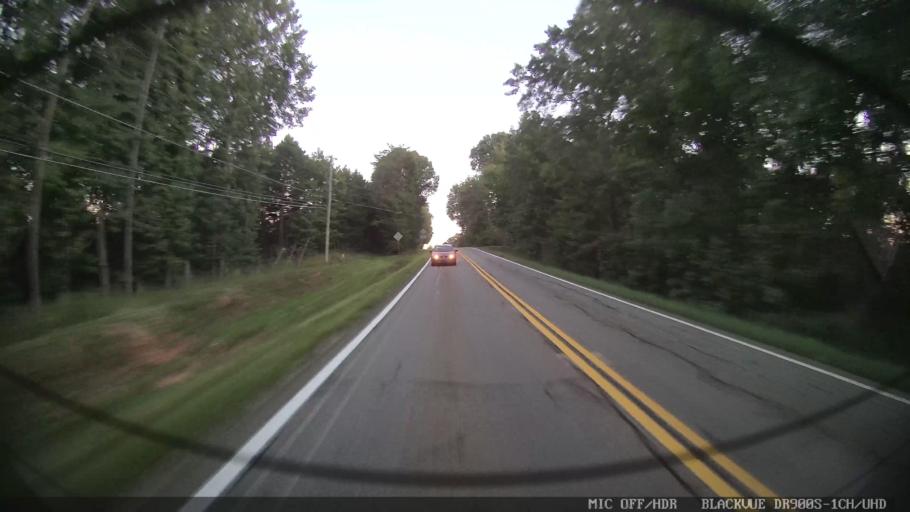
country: US
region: Georgia
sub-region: Gilmer County
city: Ellijay
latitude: 34.7326
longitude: -84.5120
